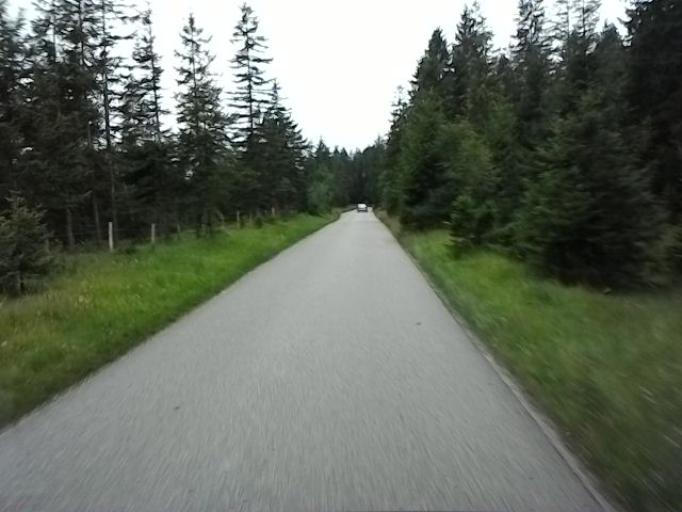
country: DE
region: Bavaria
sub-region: Upper Bavaria
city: Wallgau
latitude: 47.5335
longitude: 11.3217
